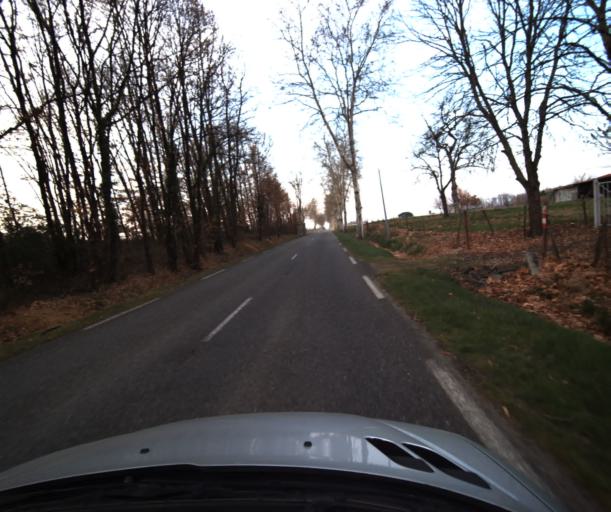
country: FR
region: Midi-Pyrenees
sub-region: Departement du Tarn-et-Garonne
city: Labastide-Saint-Pierre
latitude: 43.8793
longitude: 1.3774
